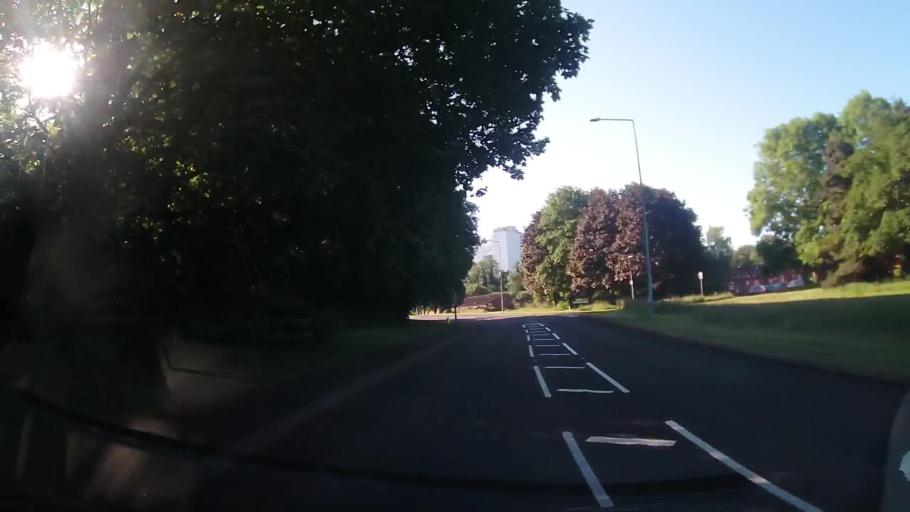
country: GB
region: England
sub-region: Shropshire
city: Hadley
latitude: 52.7069
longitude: -2.4910
